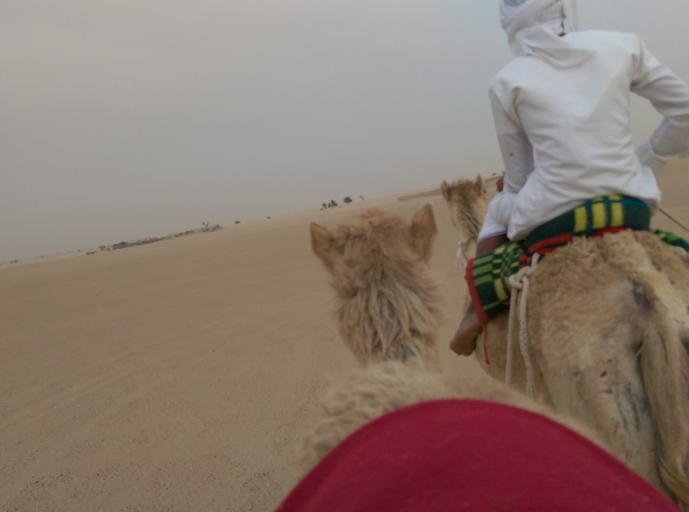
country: AE
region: Dubai
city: Dubai
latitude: 24.9350
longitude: 55.3679
